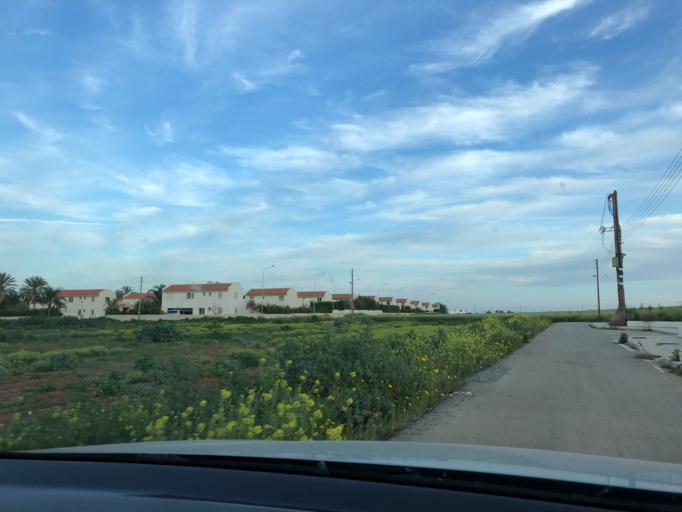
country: CY
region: Larnaka
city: Perivolia
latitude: 34.8359
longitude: 33.6006
